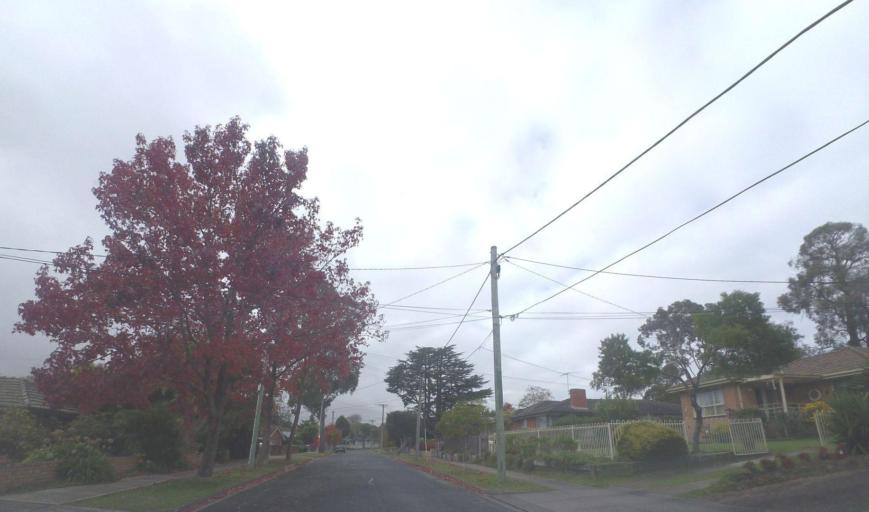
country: AU
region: Victoria
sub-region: Manningham
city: Donvale
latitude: -37.8047
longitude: 145.1839
